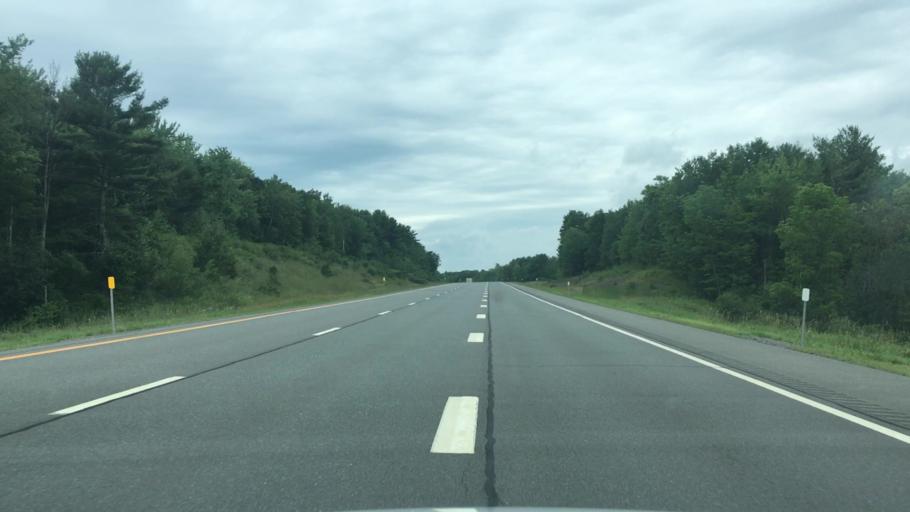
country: US
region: New York
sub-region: Schoharie County
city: Schoharie
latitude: 42.7276
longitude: -74.2040
